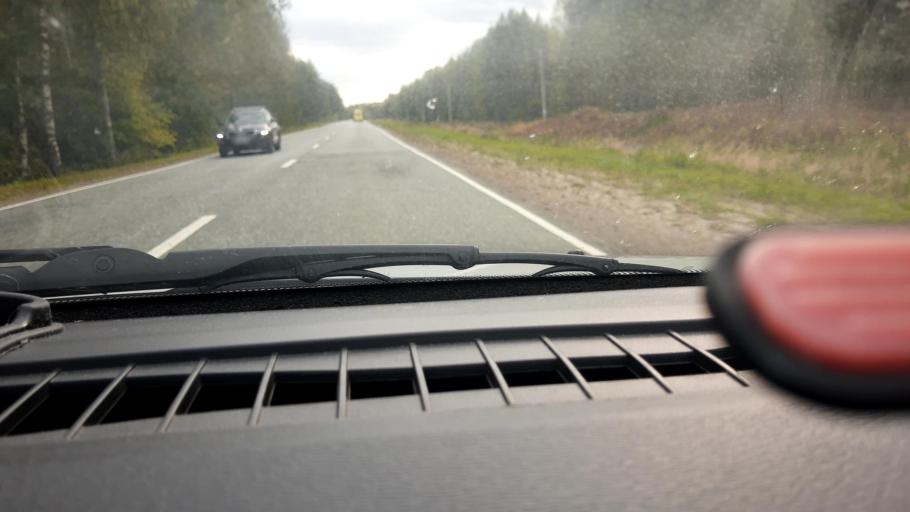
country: RU
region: Nizjnij Novgorod
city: Uren'
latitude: 57.4191
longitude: 45.6873
